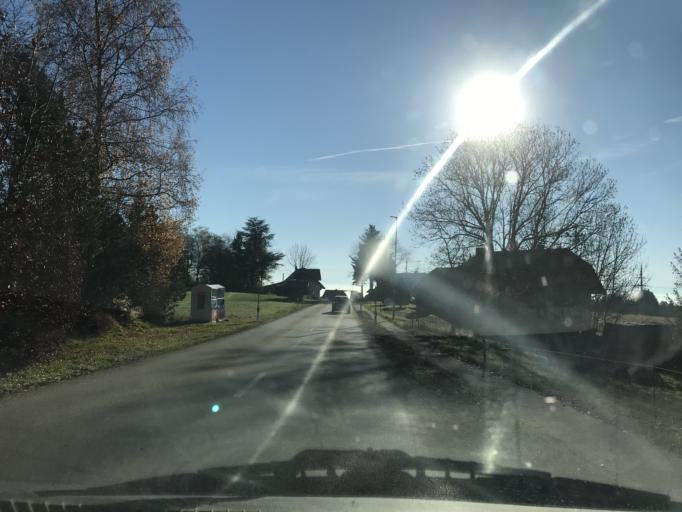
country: DE
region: Baden-Wuerttemberg
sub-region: Freiburg Region
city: Rickenbach
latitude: 47.6337
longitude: 7.9858
